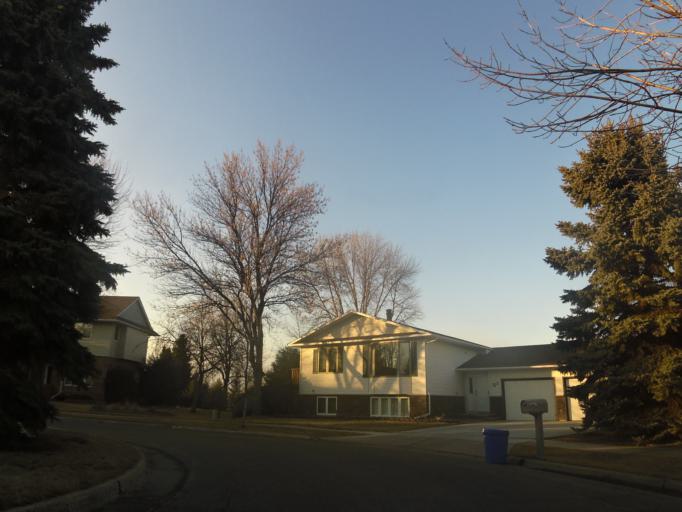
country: US
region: North Dakota
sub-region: Grand Forks County
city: Grand Forks
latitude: 47.8784
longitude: -97.0215
